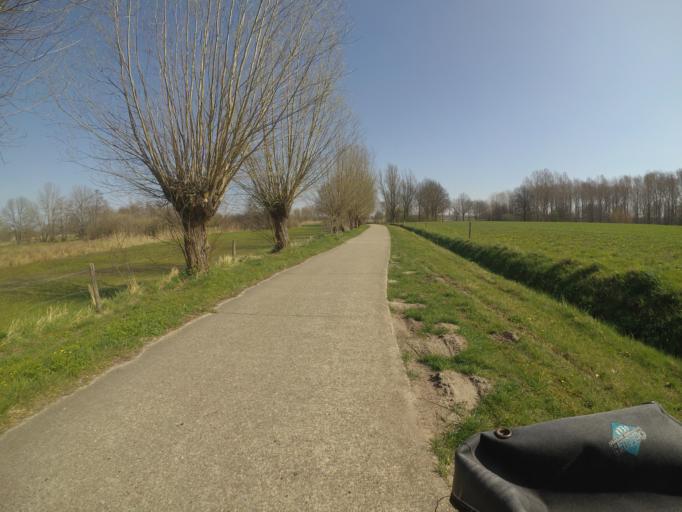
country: NL
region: North Brabant
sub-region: Gemeente Boxtel
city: Boxtel
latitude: 51.5775
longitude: 5.3894
